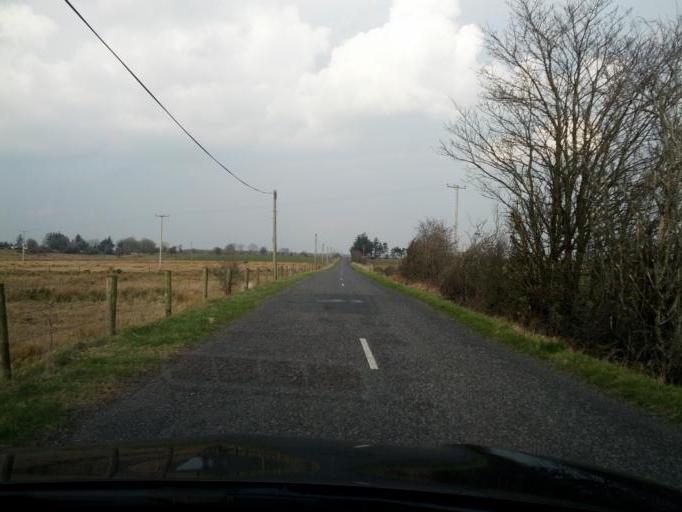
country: IE
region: Connaught
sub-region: County Galway
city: Athenry
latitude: 53.4363
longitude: -8.5666
